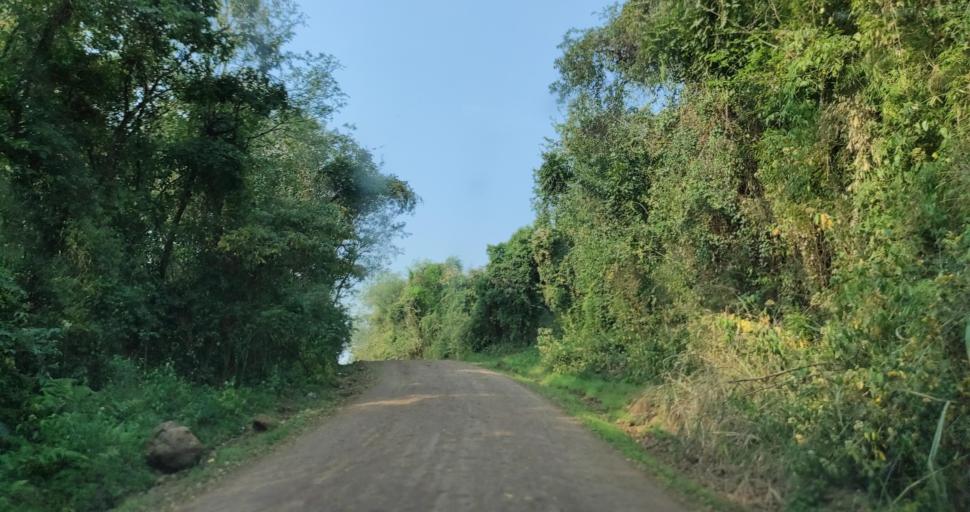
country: AR
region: Misiones
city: Cerro Azul
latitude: -27.6267
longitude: -55.5301
